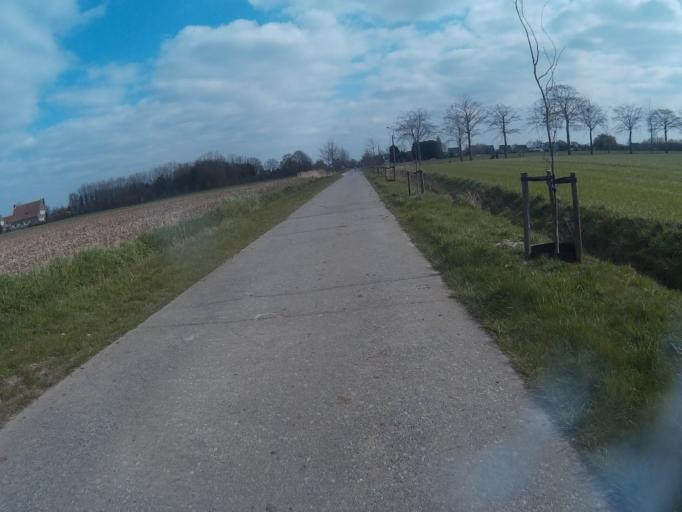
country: BE
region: Flanders
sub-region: Provincie Oost-Vlaanderen
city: Eeklo
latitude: 51.1544
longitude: 3.5299
